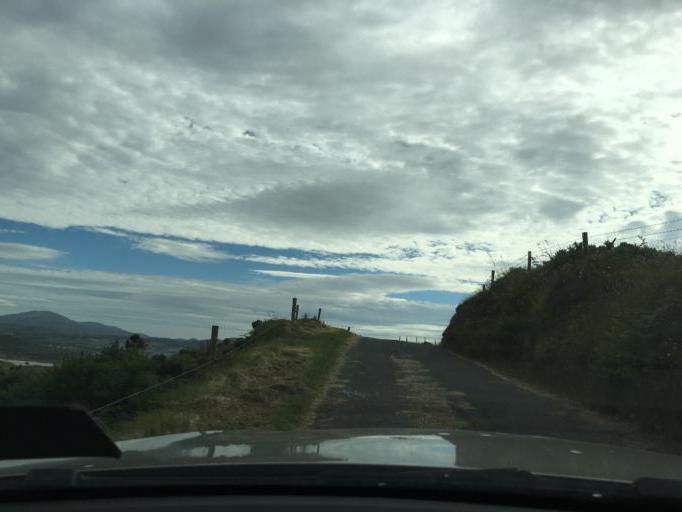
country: IE
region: Ulster
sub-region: County Donegal
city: Carndonagh
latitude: 55.3289
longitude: -7.3279
